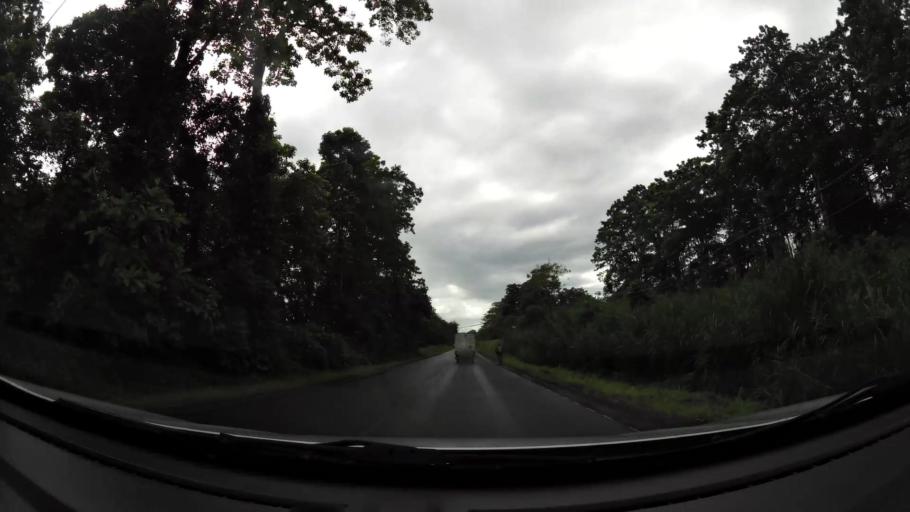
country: CR
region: Limon
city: Pocora
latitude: 10.1611
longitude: -83.5996
